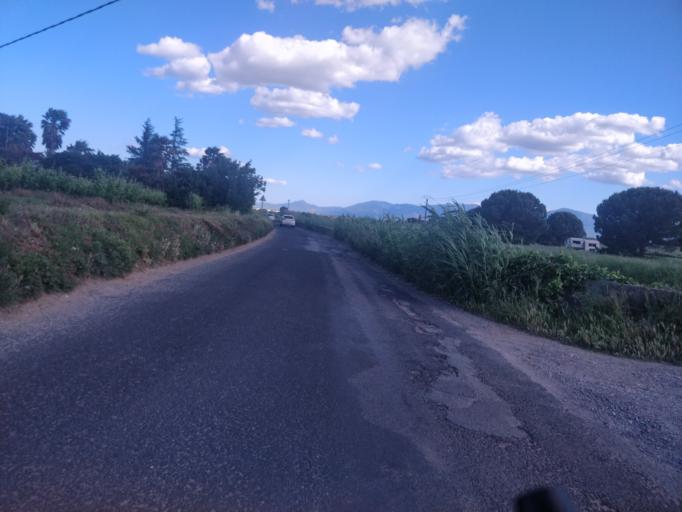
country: FR
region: Languedoc-Roussillon
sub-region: Departement des Pyrenees-Orientales
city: Cabestany
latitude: 42.6751
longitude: 2.9221
